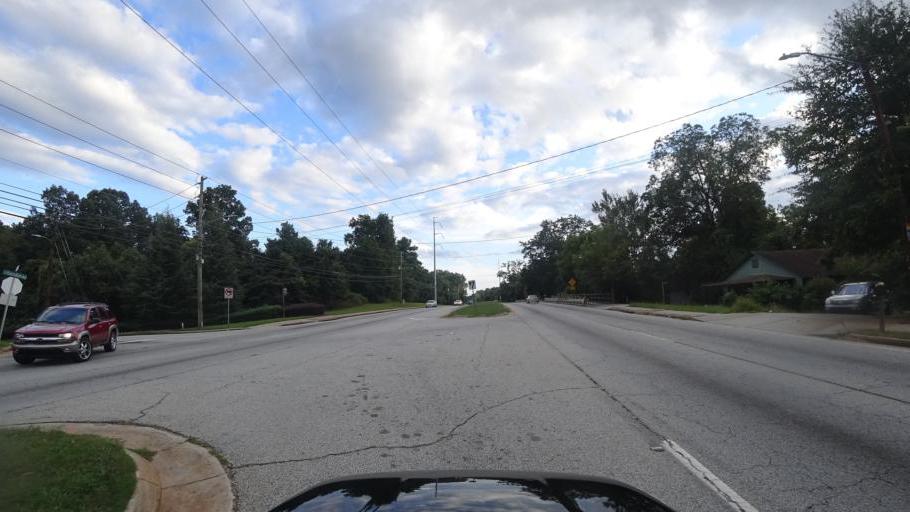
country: US
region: Georgia
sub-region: DeKalb County
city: Stone Mountain
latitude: 33.7570
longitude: -84.1971
